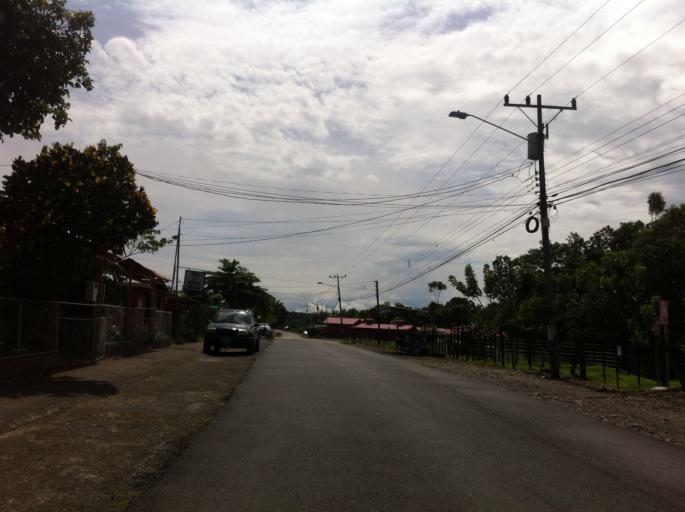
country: CR
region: San Jose
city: Dulce Nombre de Jesus
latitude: 10.3381
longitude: -83.9557
